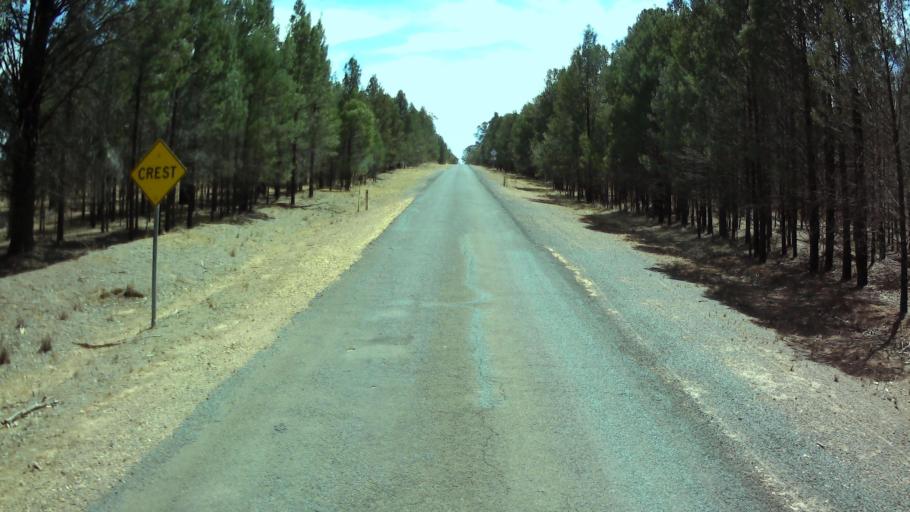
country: AU
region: New South Wales
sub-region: Weddin
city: Grenfell
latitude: -33.7615
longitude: 148.2051
